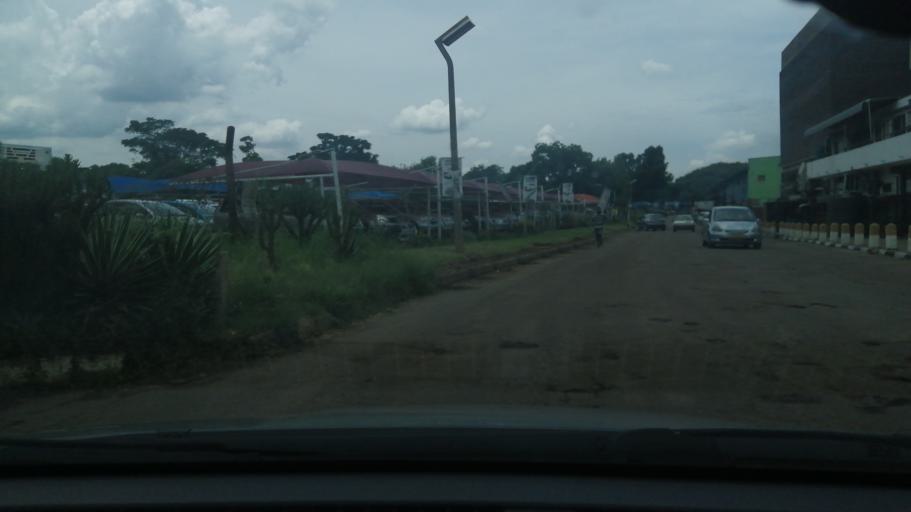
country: ZW
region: Harare
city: Harare
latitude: -17.8021
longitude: 31.0389
